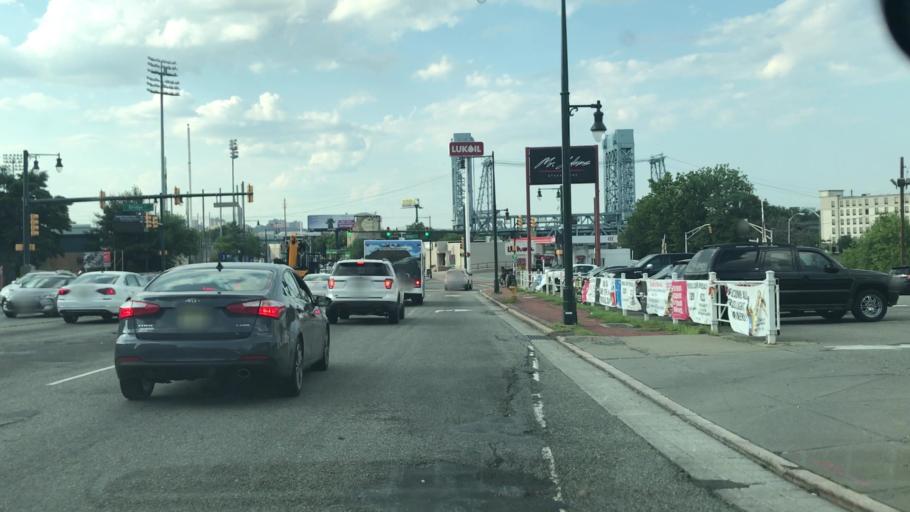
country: US
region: New Jersey
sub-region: Hudson County
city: East Newark
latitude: 40.7443
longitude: -74.1672
